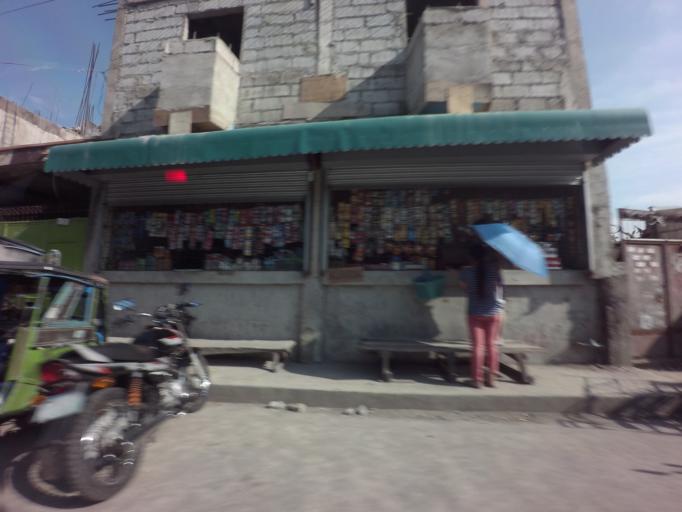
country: PH
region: Calabarzon
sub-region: Province of Rizal
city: Taguig
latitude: 14.4990
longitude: 121.0580
